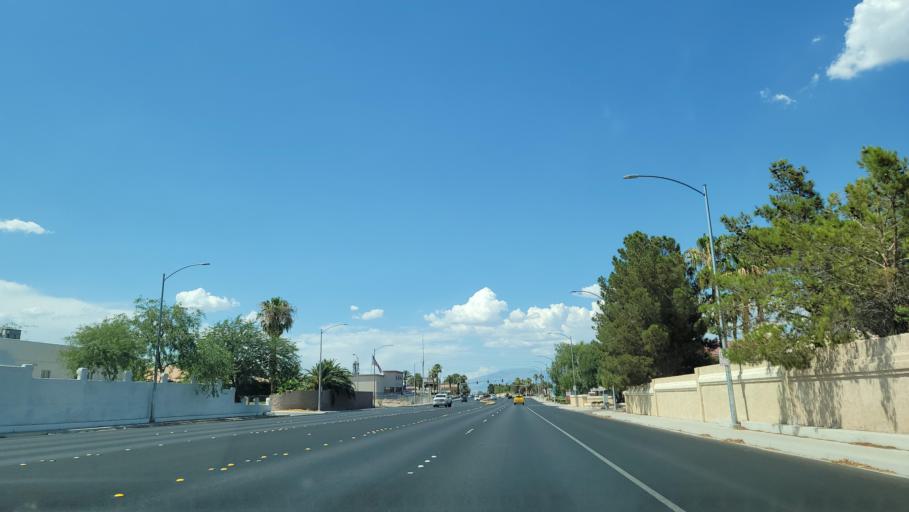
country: US
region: Nevada
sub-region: Clark County
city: Spring Valley
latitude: 36.1406
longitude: -115.2609
